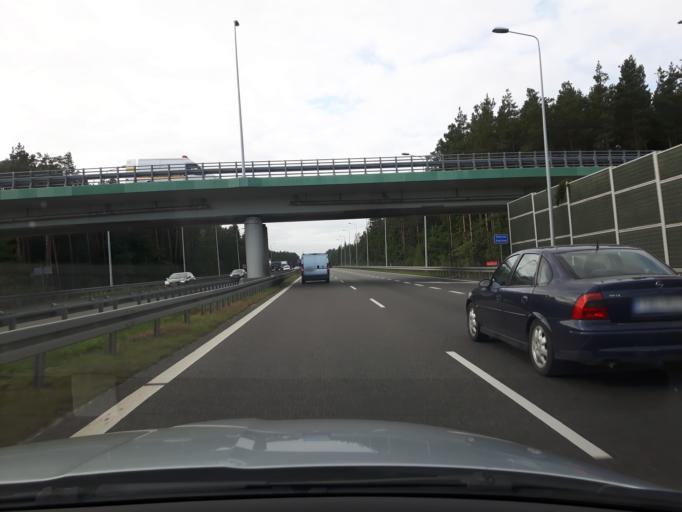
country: PL
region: Swietokrzyskie
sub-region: Powiat skarzyski
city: Suchedniow
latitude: 51.0292
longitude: 20.8171
